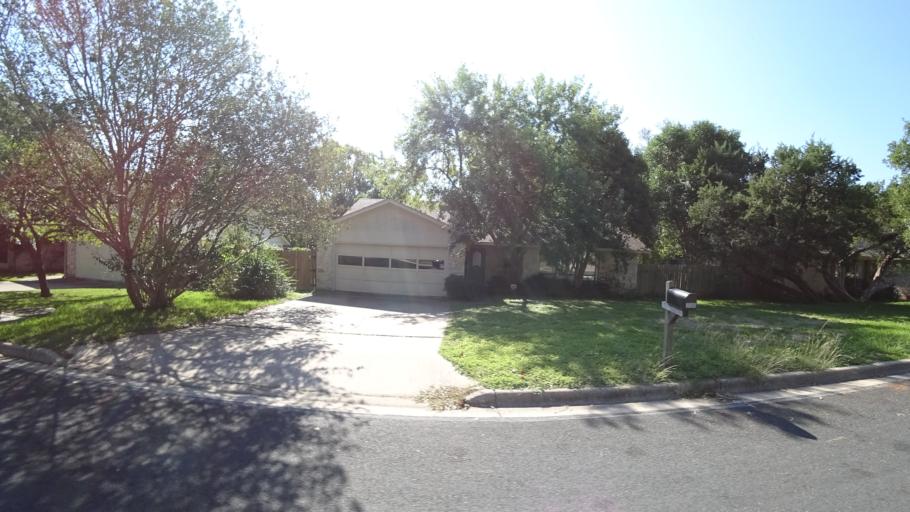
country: US
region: Texas
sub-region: Travis County
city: Rollingwood
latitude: 30.2690
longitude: -97.8100
